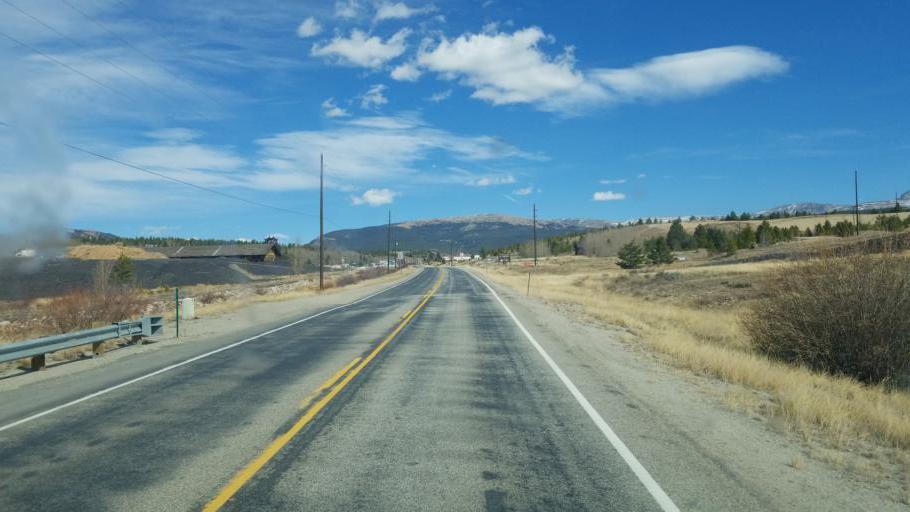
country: US
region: Colorado
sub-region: Lake County
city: Leadville North
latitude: 39.2316
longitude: -106.3217
